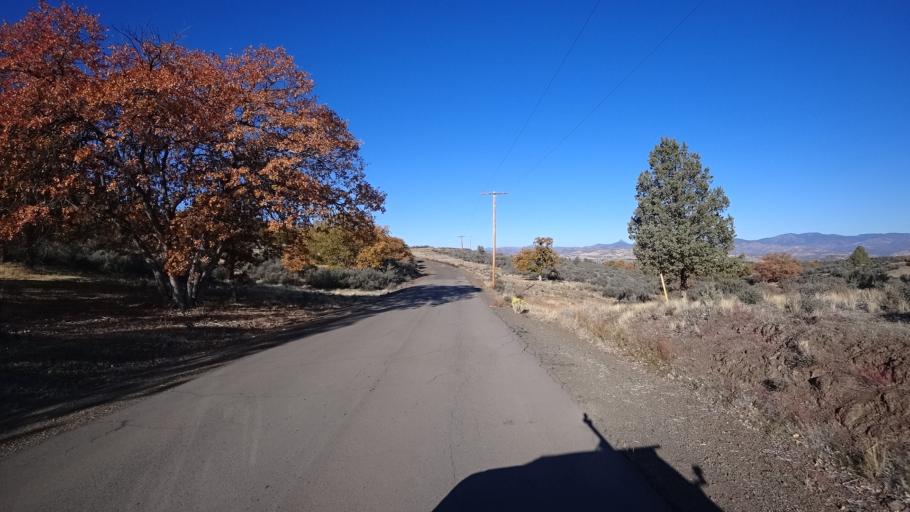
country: US
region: California
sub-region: Siskiyou County
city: Montague
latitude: 41.9031
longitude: -122.4314
